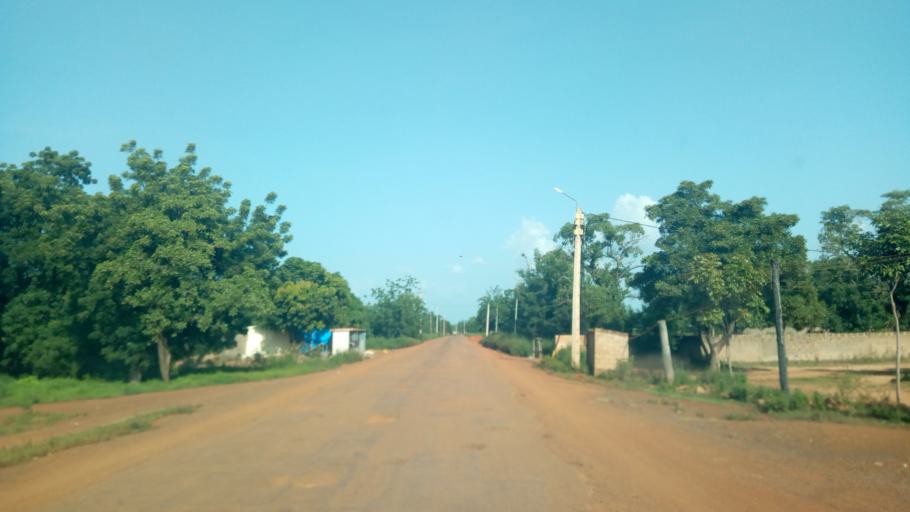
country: ML
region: Sikasso
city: Yorosso
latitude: 12.1849
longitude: -4.8163
